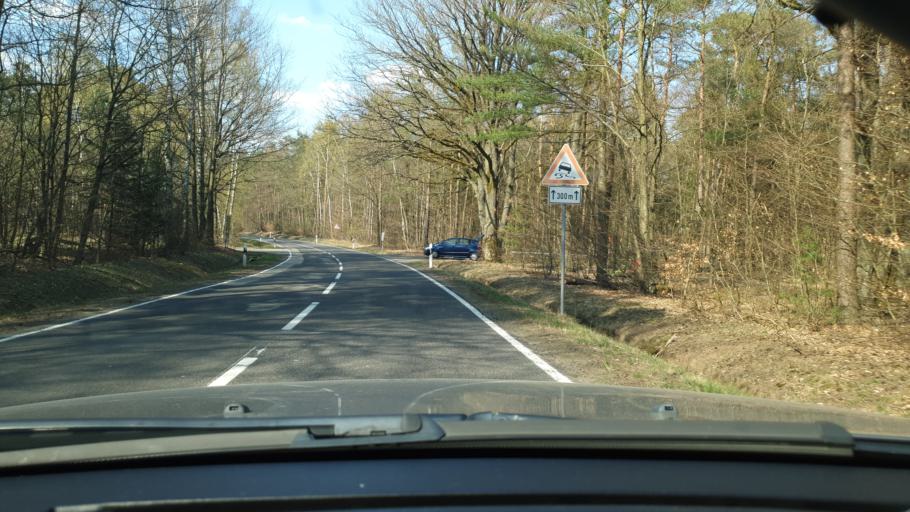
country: DE
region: Rheinland-Pfalz
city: Landstuhl
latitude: 49.3996
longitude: 7.5399
